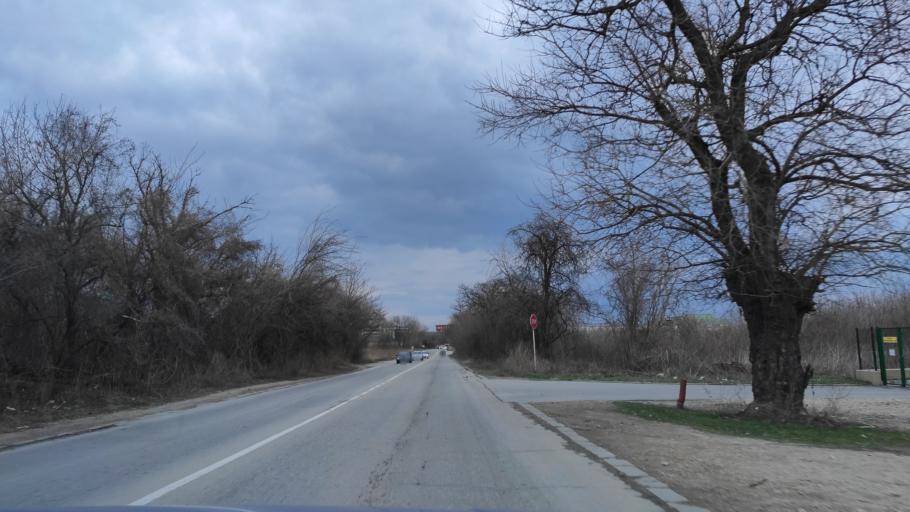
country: BG
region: Varna
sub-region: Obshtina Aksakovo
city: Aksakovo
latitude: 43.2278
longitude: 27.8484
